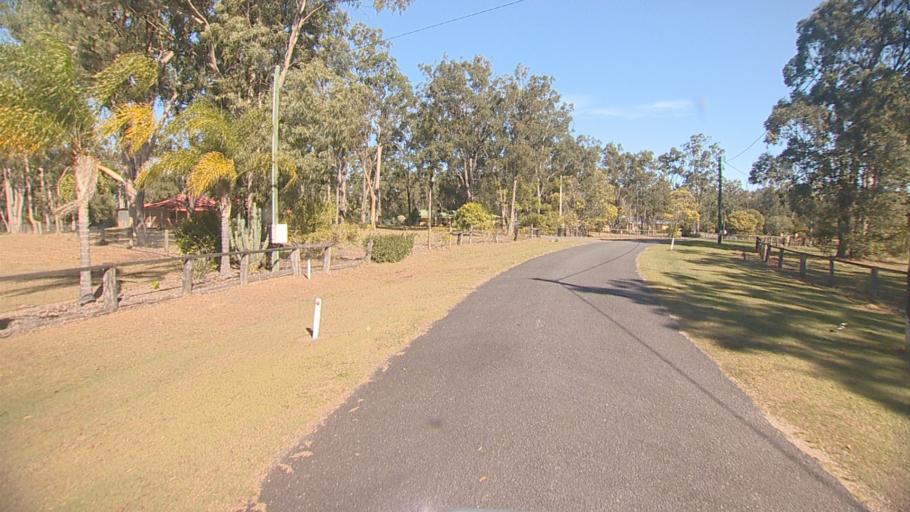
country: AU
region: Queensland
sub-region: Ipswich
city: Springfield Lakes
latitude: -27.7144
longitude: 152.9542
